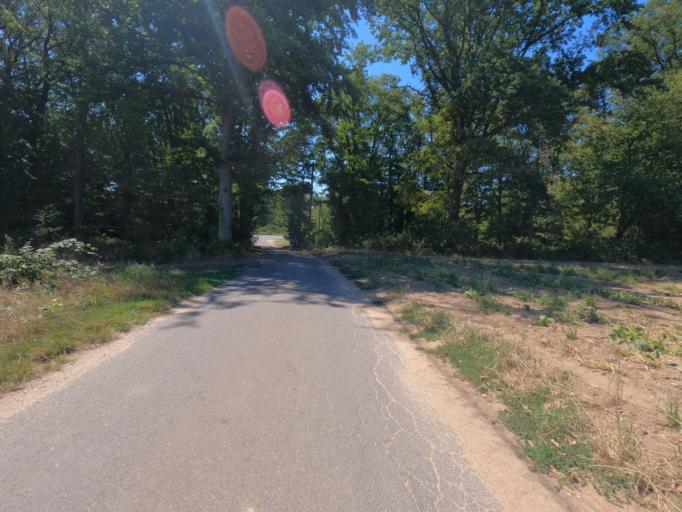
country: DE
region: North Rhine-Westphalia
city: Wegberg
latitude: 51.1624
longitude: 6.2653
